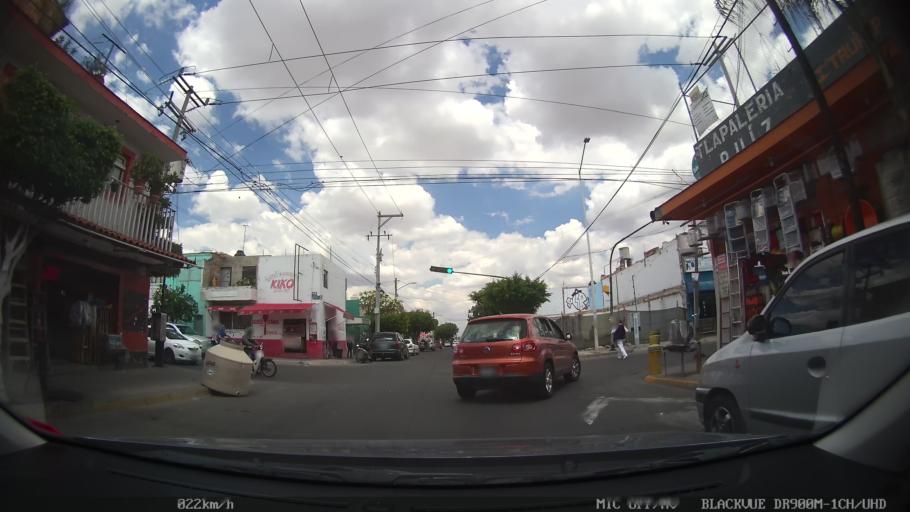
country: MX
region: Jalisco
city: Tlaquepaque
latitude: 20.6507
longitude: -103.2798
